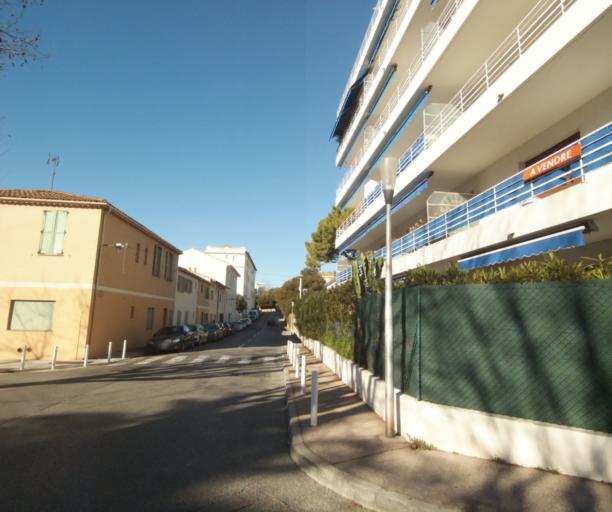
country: FR
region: Provence-Alpes-Cote d'Azur
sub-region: Departement des Alpes-Maritimes
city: Antibes
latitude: 43.5734
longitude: 7.1091
